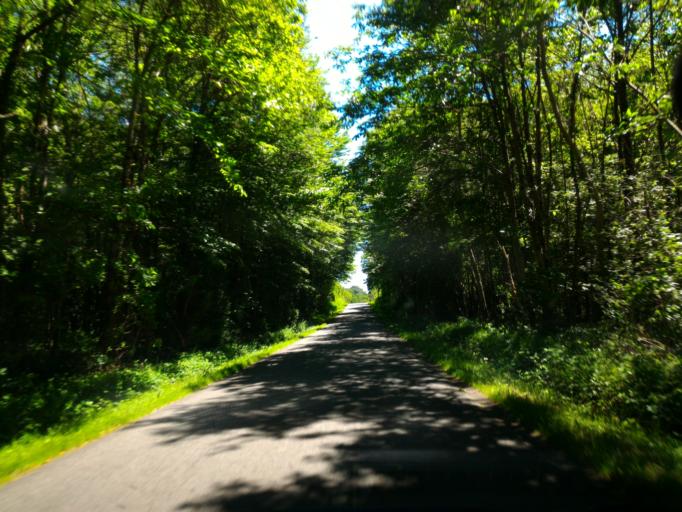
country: FR
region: Poitou-Charentes
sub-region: Departement de la Vienne
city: Availles-Limouzine
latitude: 46.0791
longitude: 0.7444
